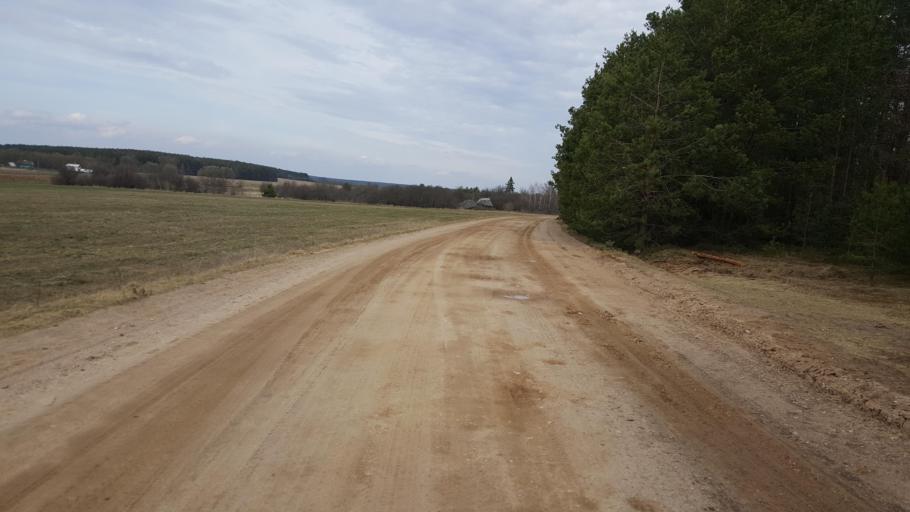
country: BY
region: Brest
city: Kamyanyets
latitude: 52.3700
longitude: 23.9778
